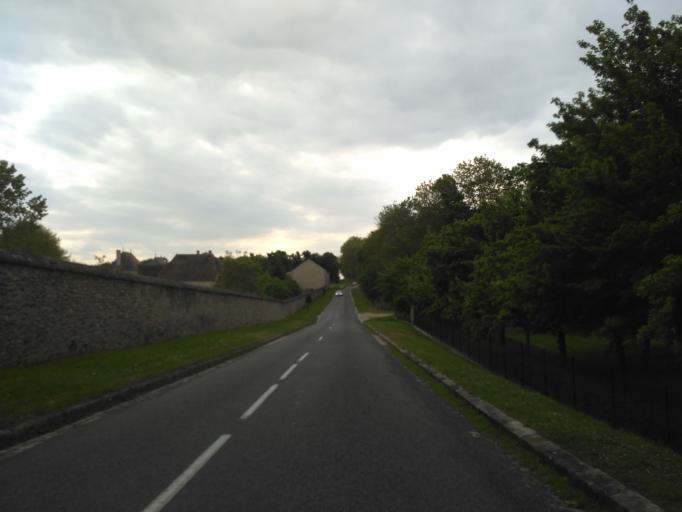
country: FR
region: Ile-de-France
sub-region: Departement de Seine-et-Marne
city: Moisenay
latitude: 48.5686
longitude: 2.7184
